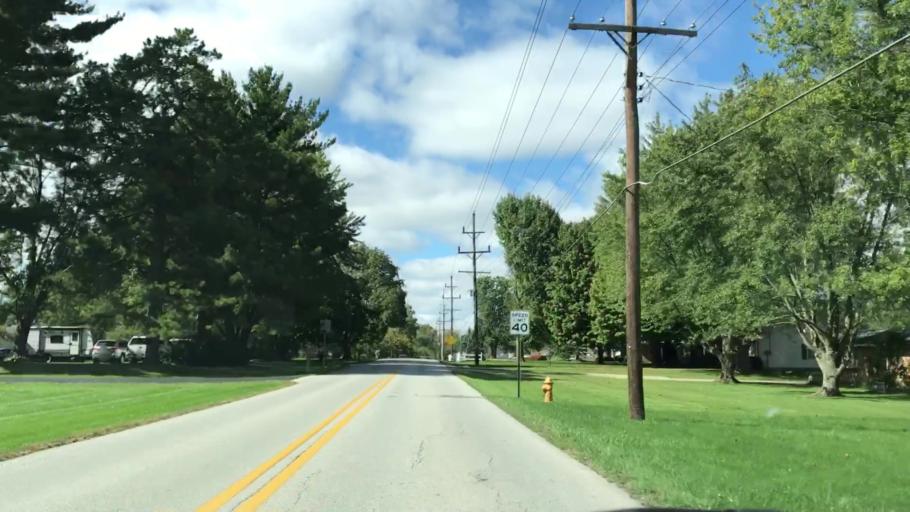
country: US
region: Indiana
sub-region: Howard County
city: Indian Heights
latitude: 40.4482
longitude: -86.1040
